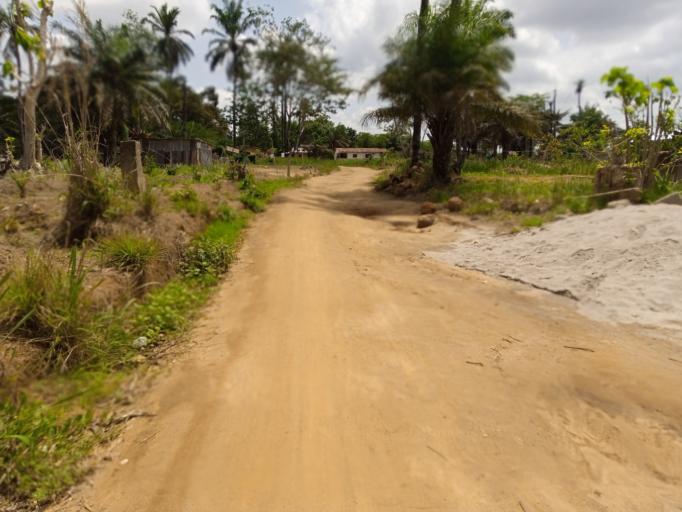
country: SL
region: Western Area
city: Waterloo
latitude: 8.3230
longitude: -13.0119
